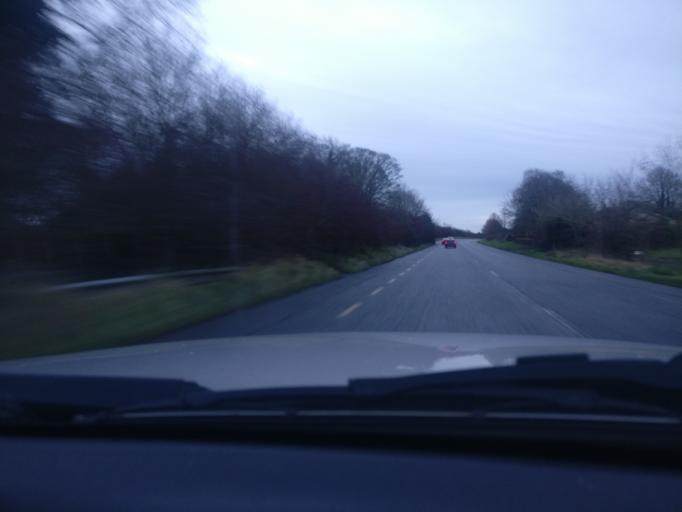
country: IE
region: Leinster
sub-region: An Mhi
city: Kells
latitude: 53.7006
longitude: -6.7917
